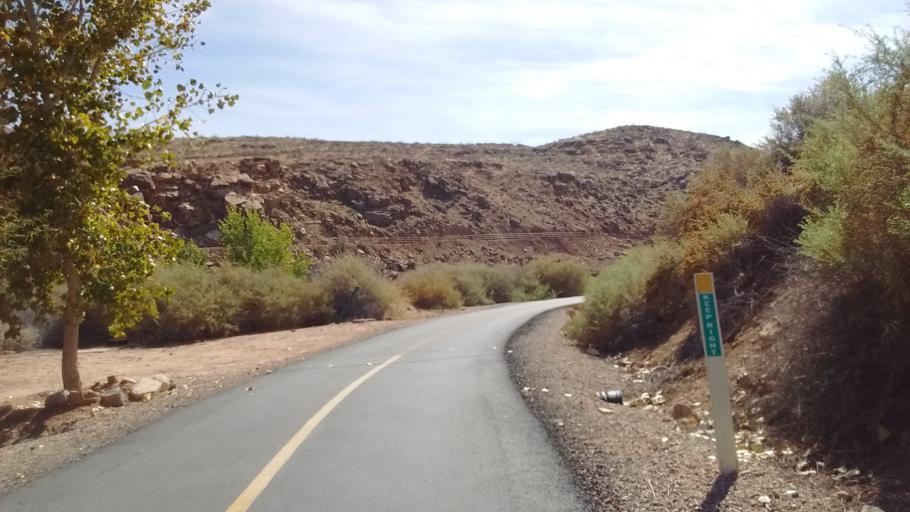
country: US
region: Utah
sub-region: Washington County
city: Saint George
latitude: 37.0721
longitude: -113.5818
